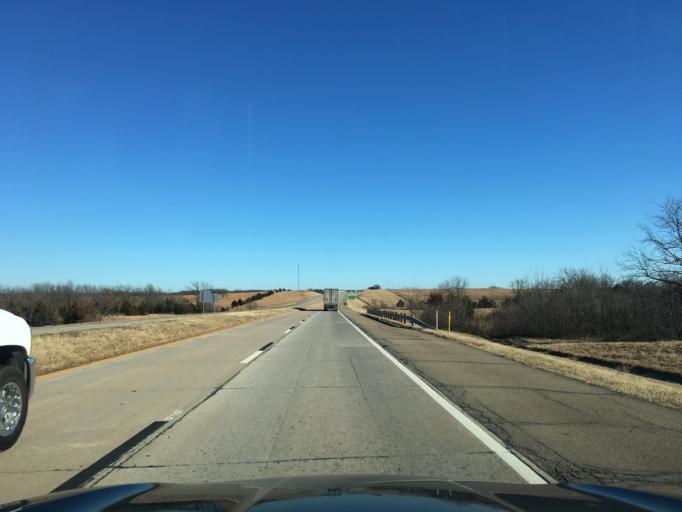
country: US
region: Oklahoma
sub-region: Pawnee County
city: Pawnee
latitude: 36.2248
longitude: -96.7694
